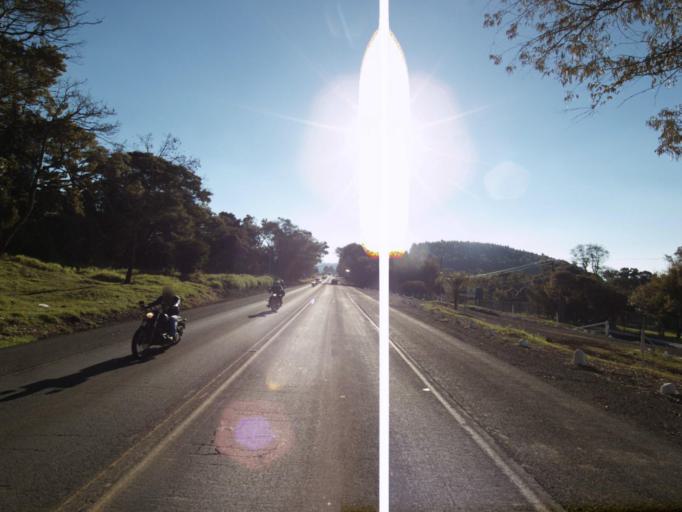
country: BR
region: Santa Catarina
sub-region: Chapeco
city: Chapeco
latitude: -26.9757
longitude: -52.7419
